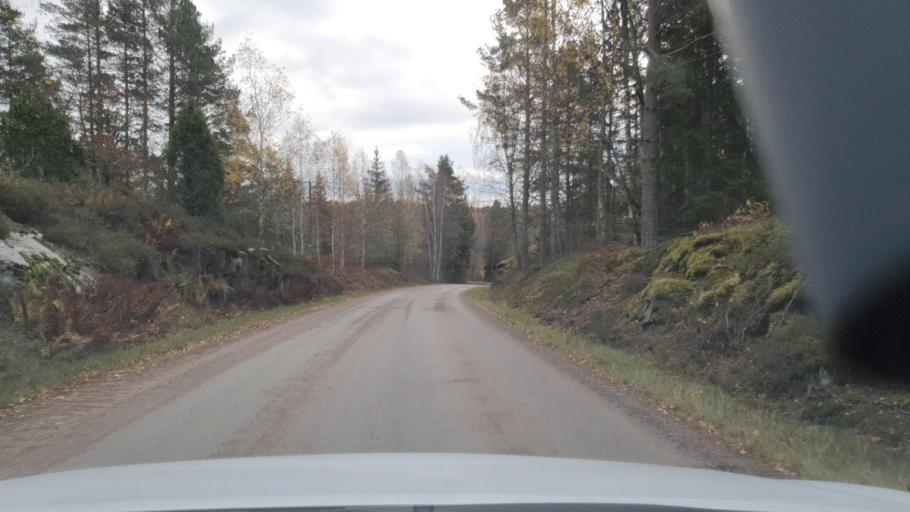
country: SE
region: Kalmar
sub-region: Vasterviks Kommun
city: Ankarsrum
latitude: 57.6961
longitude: 16.4634
